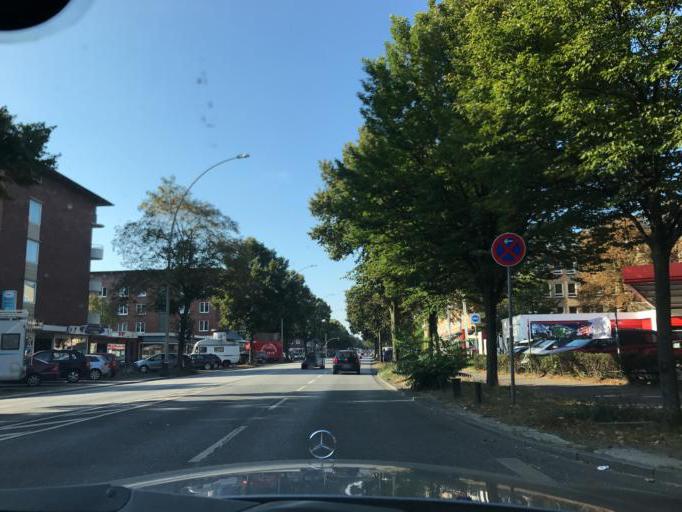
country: DE
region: Hamburg
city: Hamburg
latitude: 53.5689
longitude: 10.0247
